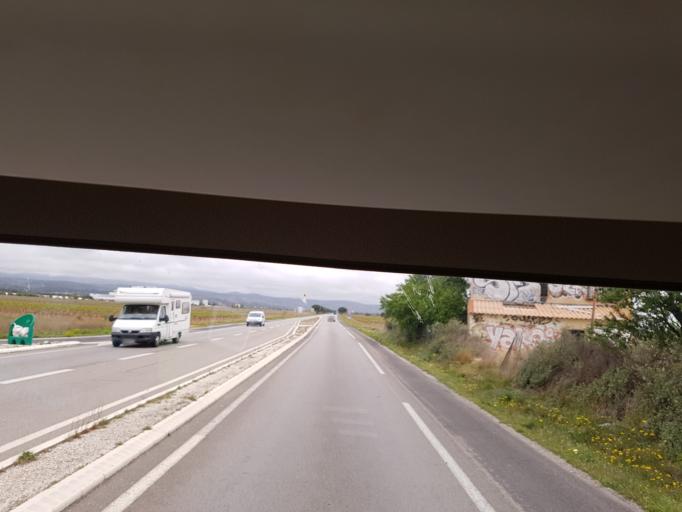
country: FR
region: Languedoc-Roussillon
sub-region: Departement des Pyrenees-Orientales
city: Salses-le-Chateau
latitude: 42.7998
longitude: 2.9099
